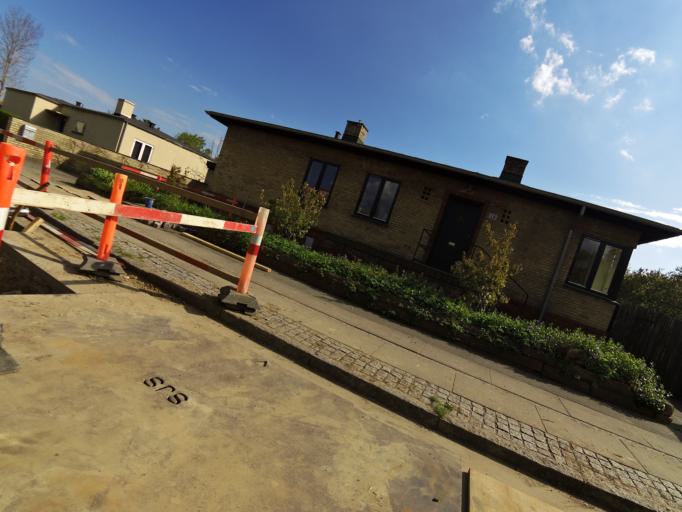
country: DK
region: Capital Region
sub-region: Lyngby-Tarbaek Kommune
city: Kongens Lyngby
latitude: 55.7287
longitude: 12.5269
